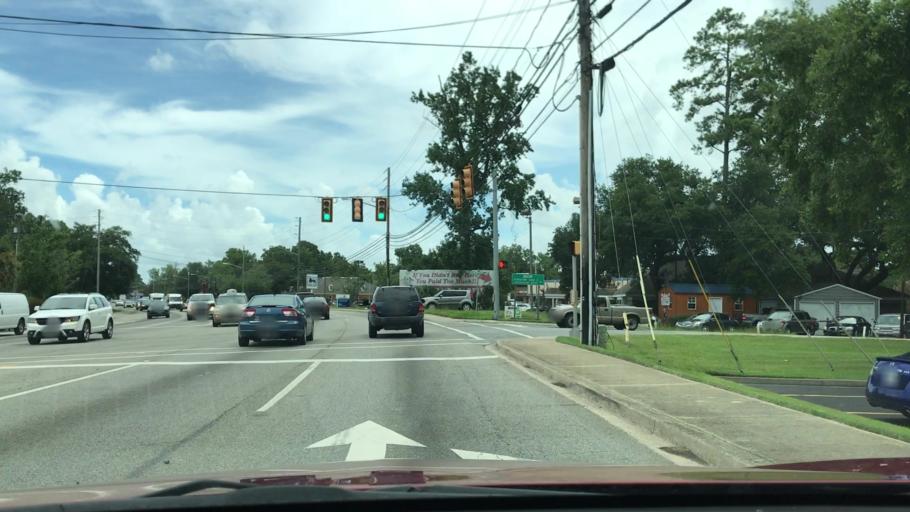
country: US
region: South Carolina
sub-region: Georgetown County
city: Georgetown
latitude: 33.3879
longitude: -79.2891
